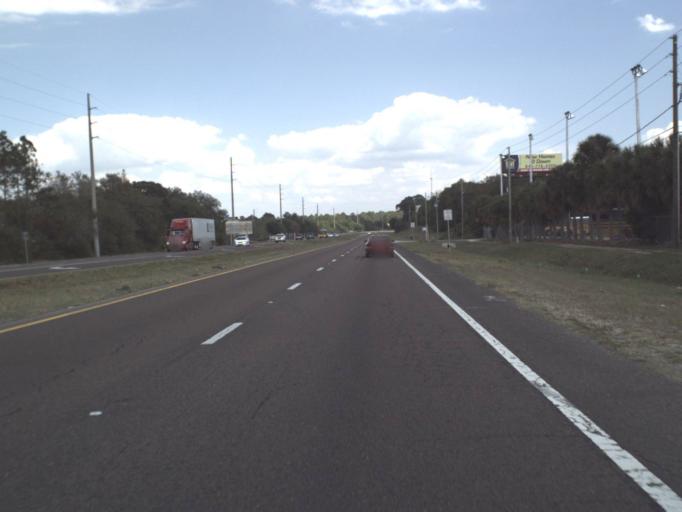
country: US
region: Florida
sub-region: Lake County
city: Howie In The Hills
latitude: 28.6405
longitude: -81.7965
